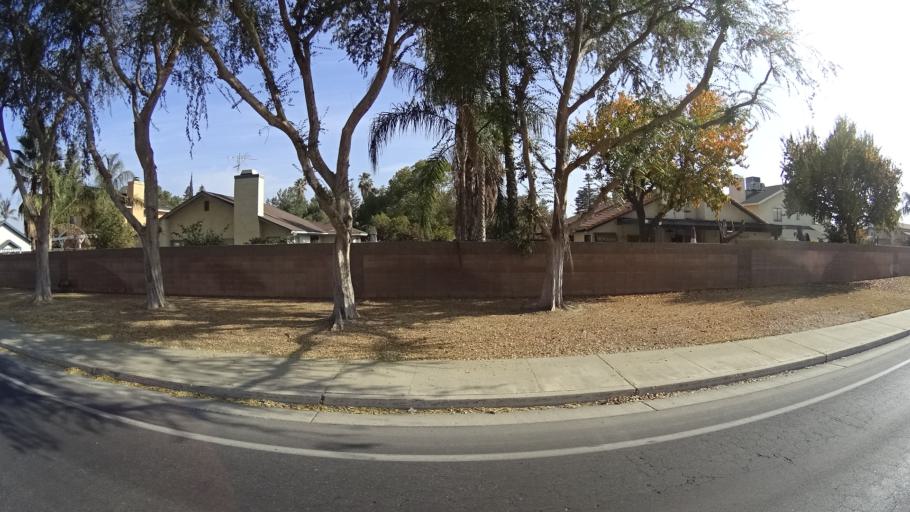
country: US
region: California
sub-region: Kern County
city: Greenacres
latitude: 35.3214
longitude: -119.1093
